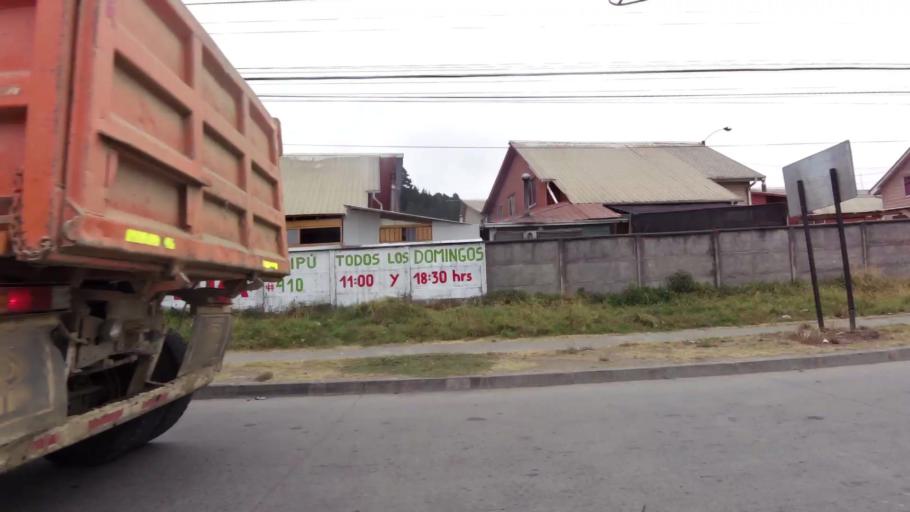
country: CL
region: Biobio
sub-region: Provincia de Concepcion
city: Concepcion
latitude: -36.8228
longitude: -72.9936
